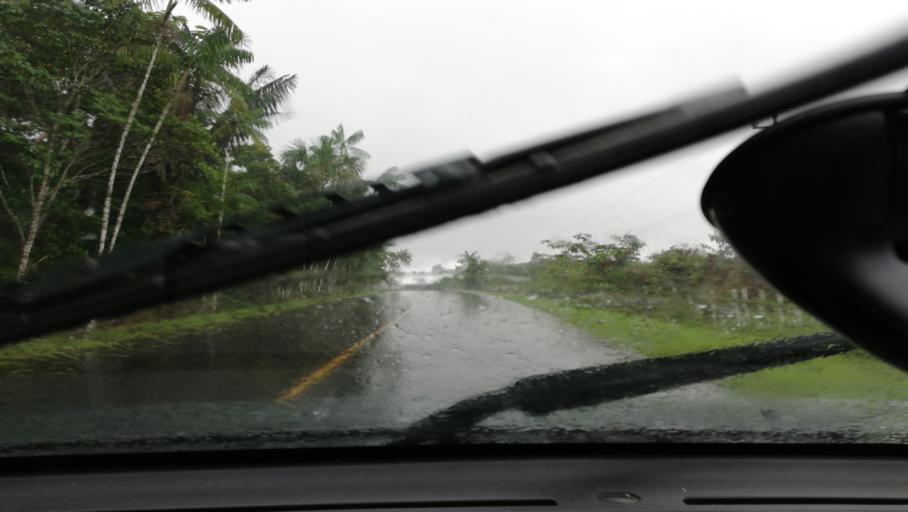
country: PE
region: Loreto
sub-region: Provincia de Maynas
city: San Juan
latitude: -3.9425
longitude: -73.3971
